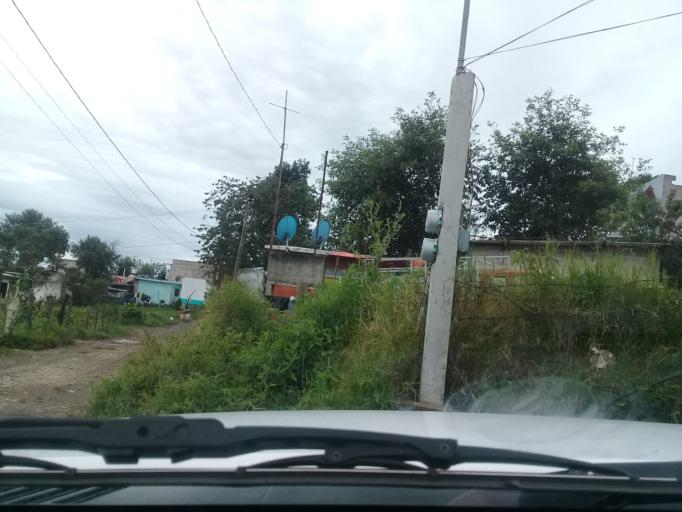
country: MX
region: Veracruz
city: Rafael Lucio
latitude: 19.5950
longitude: -96.9851
